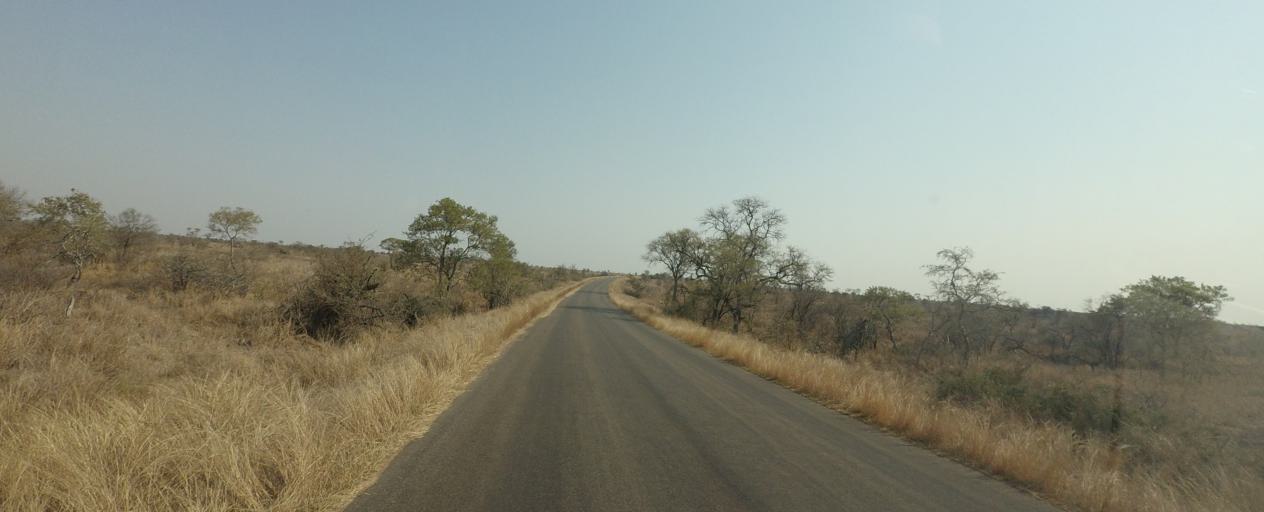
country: ZA
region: Limpopo
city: Thulamahashi
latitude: -24.3641
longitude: 31.7638
